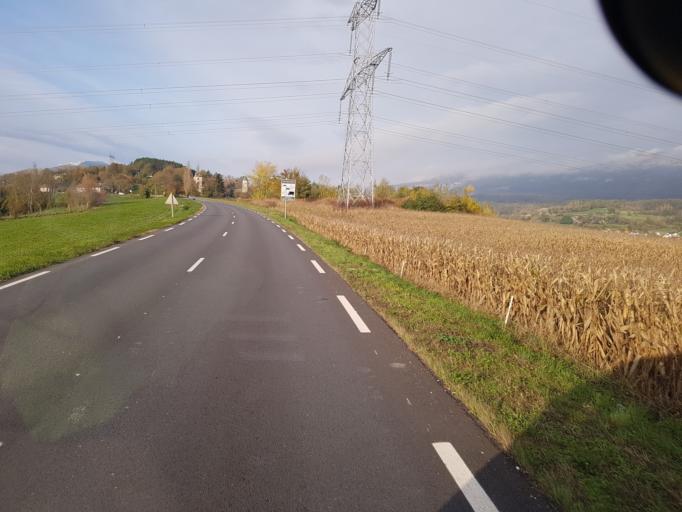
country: FR
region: Rhone-Alpes
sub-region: Departement de la Haute-Savoie
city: Frangy
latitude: 46.0372
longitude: 5.8886
